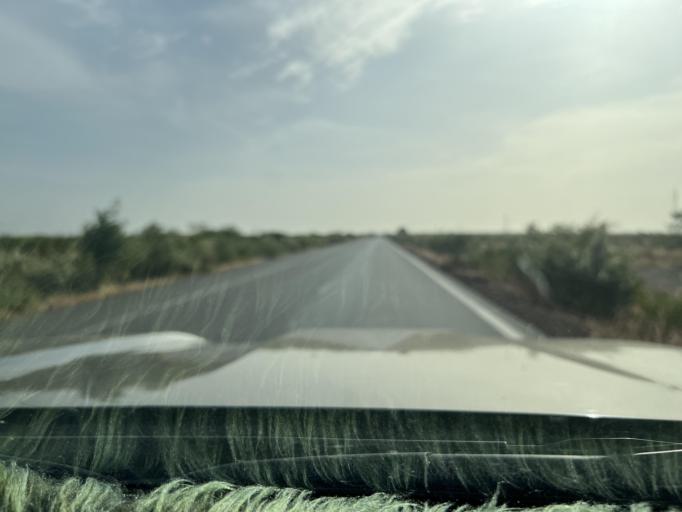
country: ML
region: Segou
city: Baroueli
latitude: 12.9609
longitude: -6.7236
